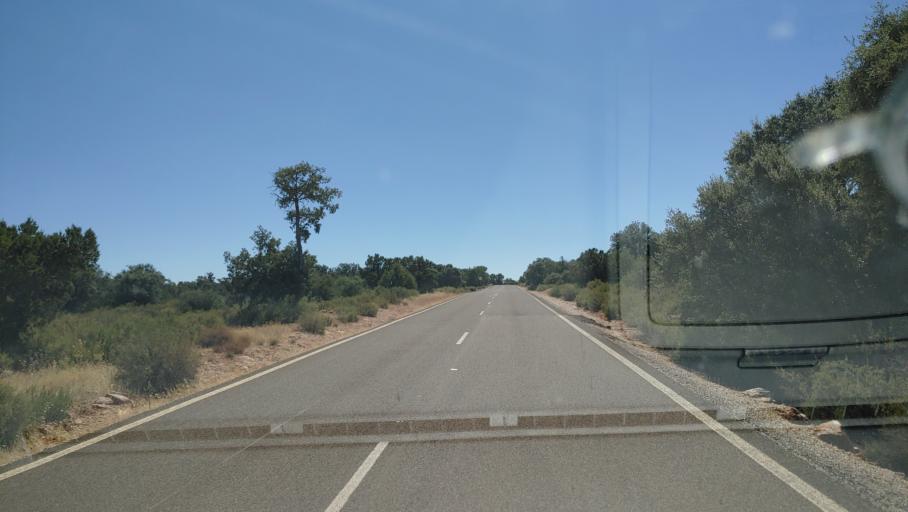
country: ES
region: Castille-La Mancha
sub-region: Provincia de Ciudad Real
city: Villahermosa
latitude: 38.8471
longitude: -2.8084
